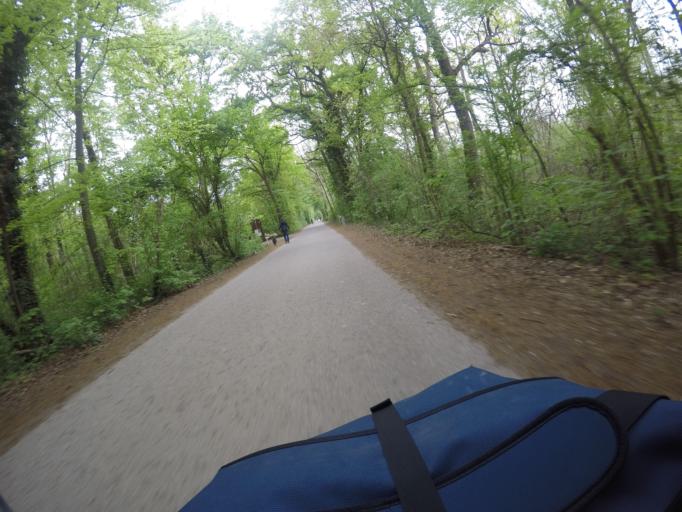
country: FR
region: Alsace
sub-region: Departement du Bas-Rhin
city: La Wantzenau
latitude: 48.6498
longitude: 7.8293
